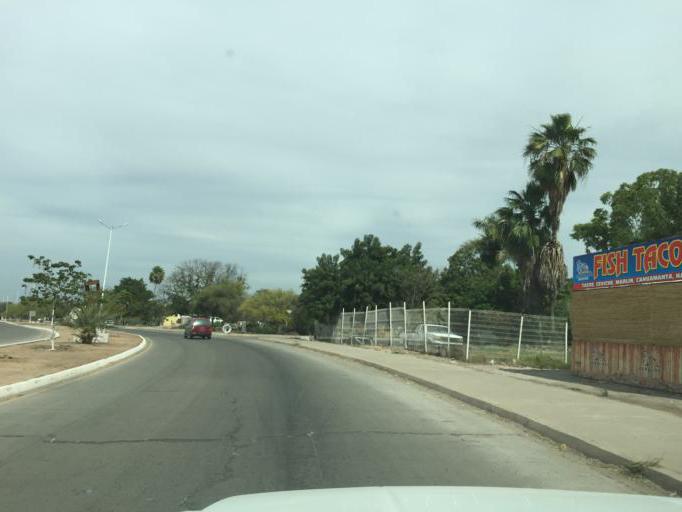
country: MX
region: Sonora
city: Navojoa
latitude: 27.0835
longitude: -109.4571
